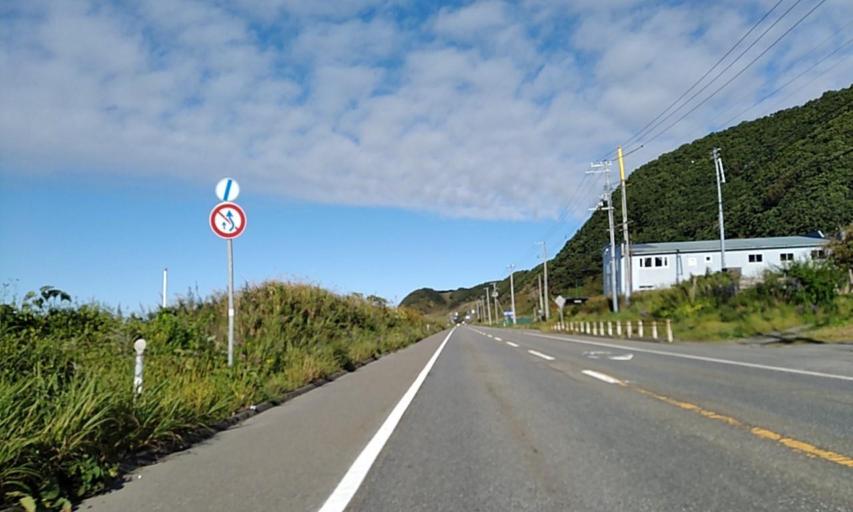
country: JP
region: Hokkaido
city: Shizunai-furukawacho
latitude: 42.3142
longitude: 142.4009
